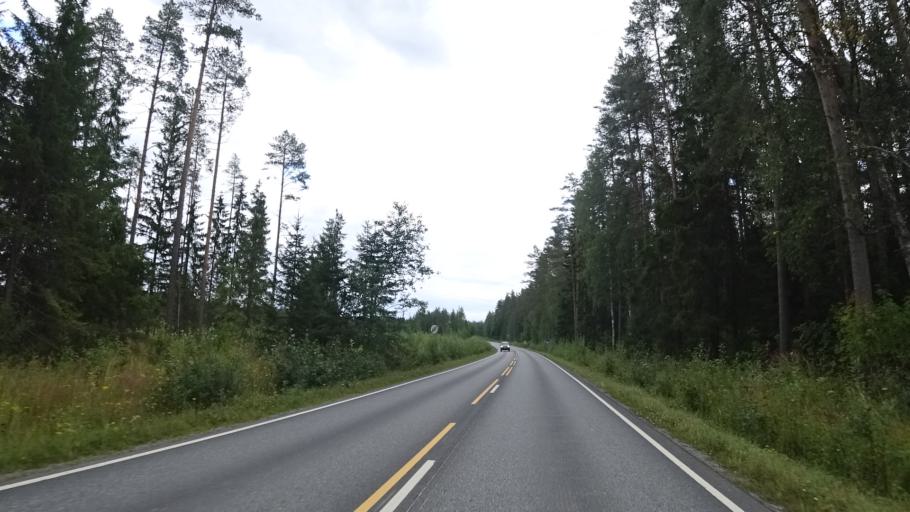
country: FI
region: North Karelia
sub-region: Joensuu
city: Ilomantsi
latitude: 62.6515
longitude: 30.9714
